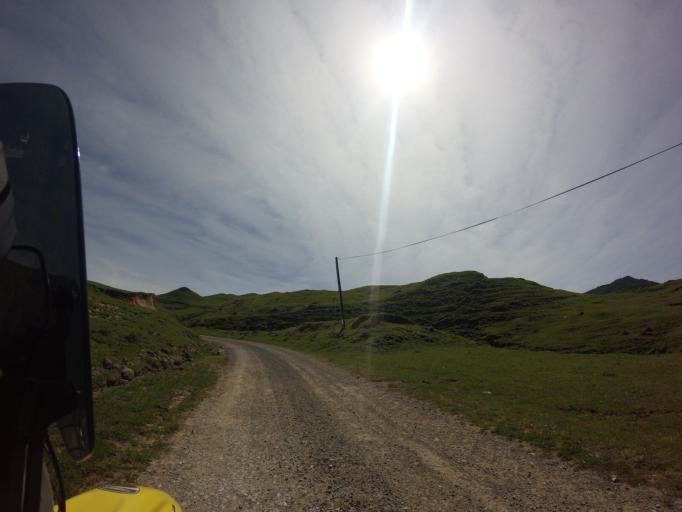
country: NZ
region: Bay of Plenty
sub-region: Opotiki District
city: Opotiki
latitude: -38.4539
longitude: 177.3661
